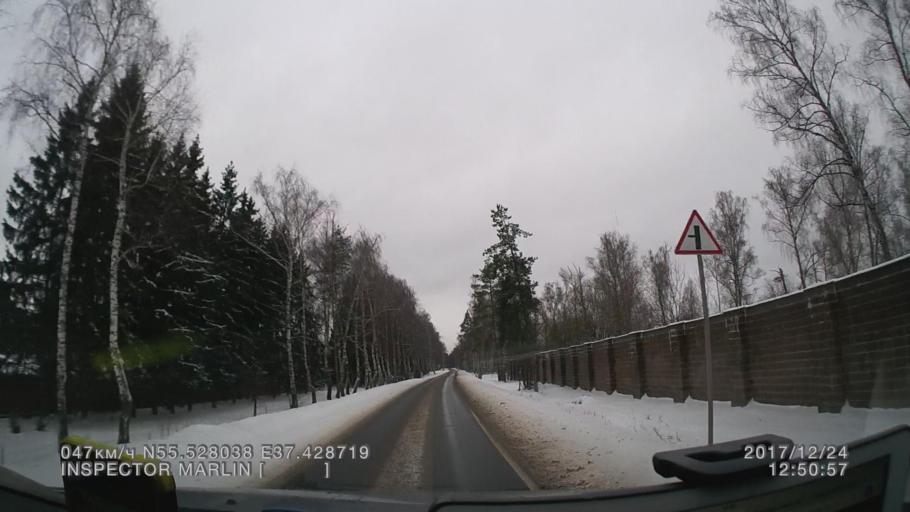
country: RU
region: Moskovskaya
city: Kommunarka
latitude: 55.5281
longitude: 37.4287
